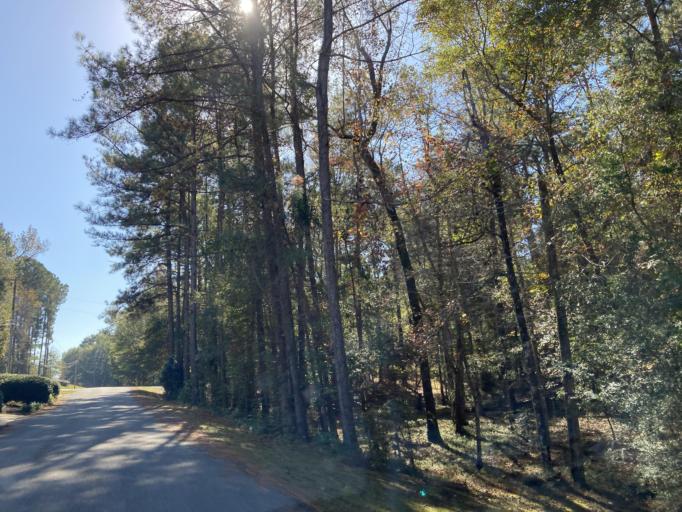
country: US
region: Mississippi
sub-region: Lamar County
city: West Hattiesburg
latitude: 31.3017
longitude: -89.4199
